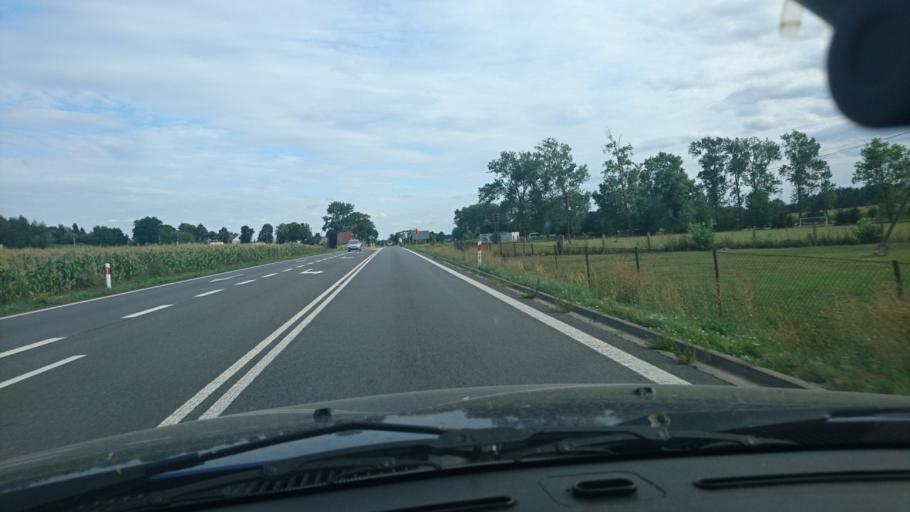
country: PL
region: Greater Poland Voivodeship
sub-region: Powiat ostrzeszowski
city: Ostrzeszow
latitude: 51.3893
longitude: 17.9465
